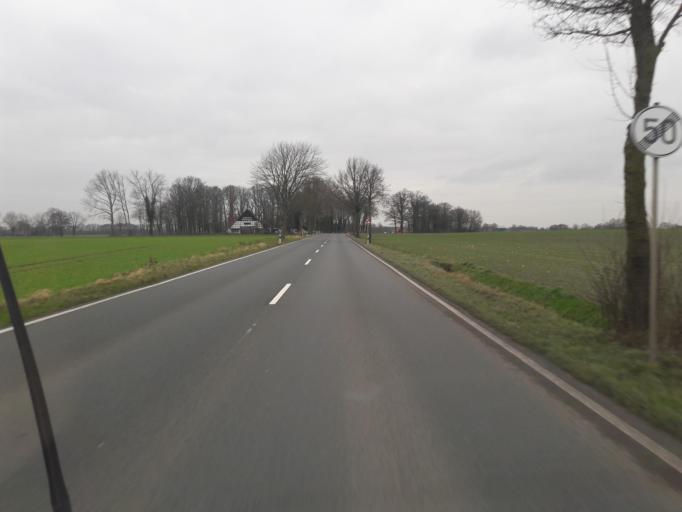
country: DE
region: Lower Saxony
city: Warmsen
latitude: 52.3651
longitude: 8.8485
